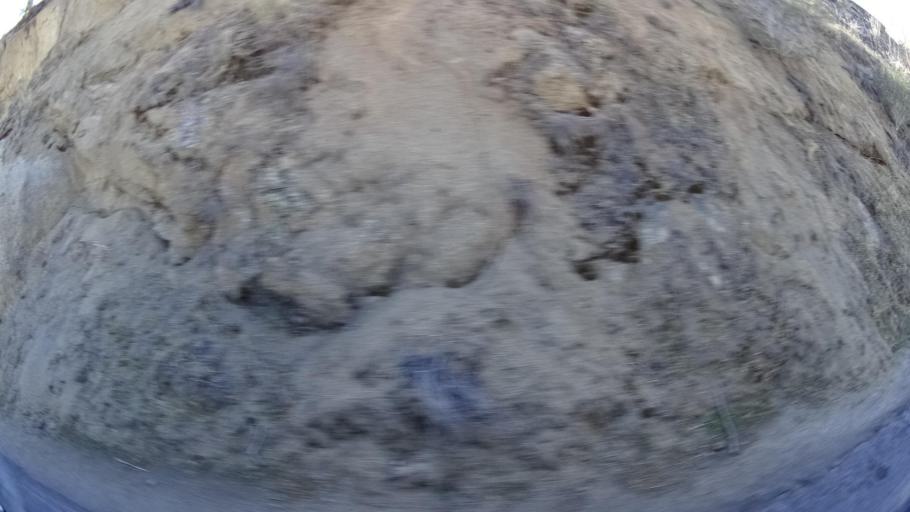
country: US
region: California
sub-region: Kern County
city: Bodfish
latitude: 35.5524
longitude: -118.5965
